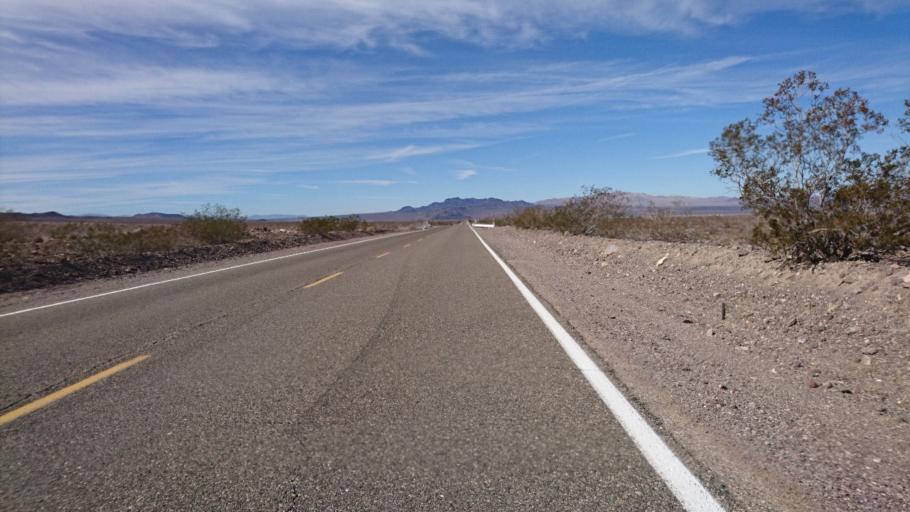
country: US
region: California
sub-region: San Bernardino County
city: Twentynine Palms
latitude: 34.7126
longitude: -116.0962
